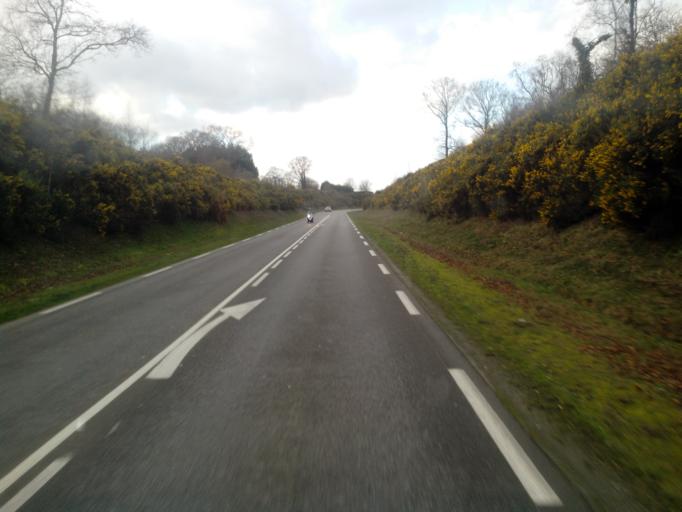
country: FR
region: Brittany
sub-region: Departement d'Ille-et-Vilaine
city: Pleurtuit
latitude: 48.5681
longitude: -2.0629
